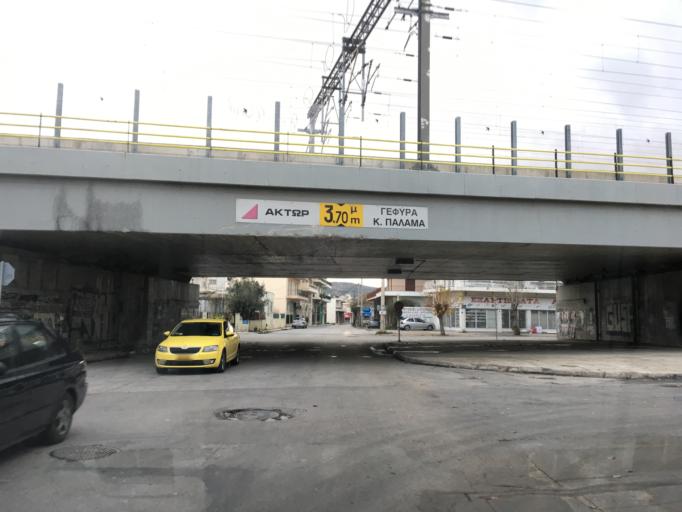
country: GR
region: Attica
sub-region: Nomarchia Athinas
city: Nea Filadelfeia
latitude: 38.0514
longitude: 23.7324
